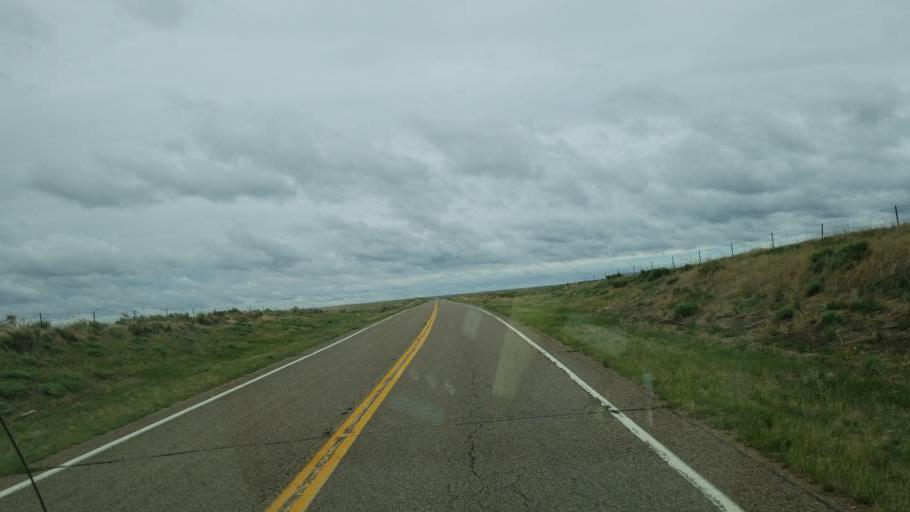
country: US
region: Colorado
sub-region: Lincoln County
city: Hugo
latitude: 38.8505
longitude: -103.5153
